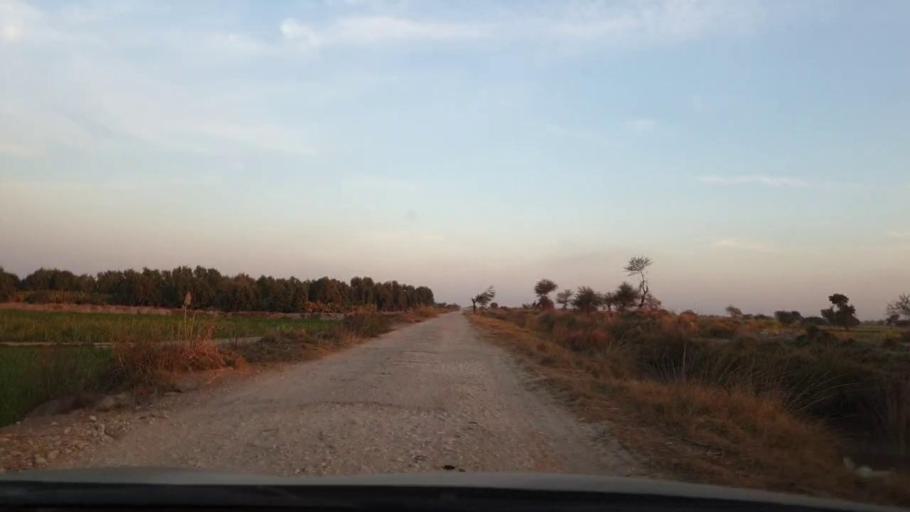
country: PK
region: Sindh
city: Tando Allahyar
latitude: 25.5850
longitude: 68.7207
